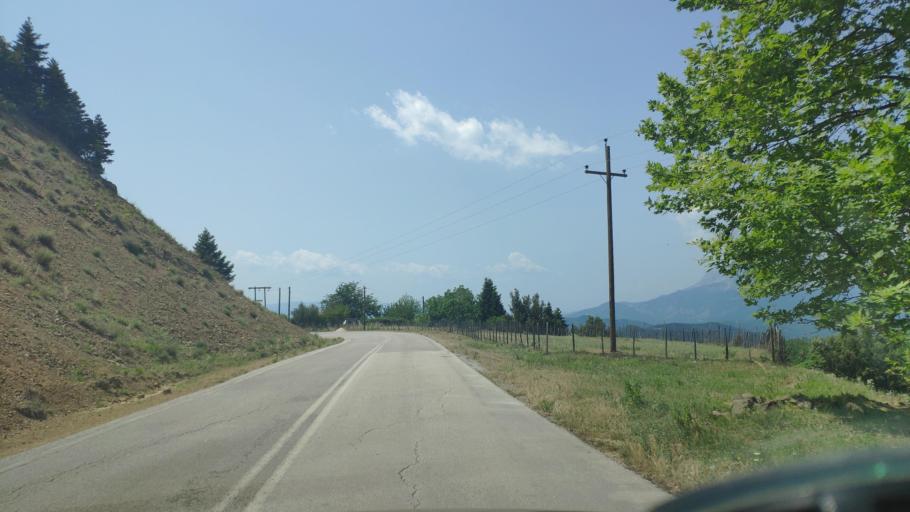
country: GR
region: Epirus
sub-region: Nomos Artas
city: Ano Kalentini
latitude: 39.2388
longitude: 21.2177
